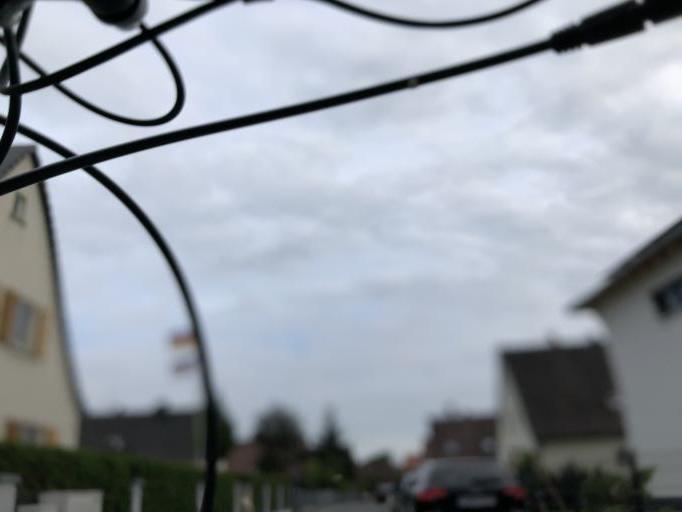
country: DE
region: Bavaria
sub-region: Regierungsbezirk Mittelfranken
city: Erlangen
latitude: 49.5353
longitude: 11.0253
